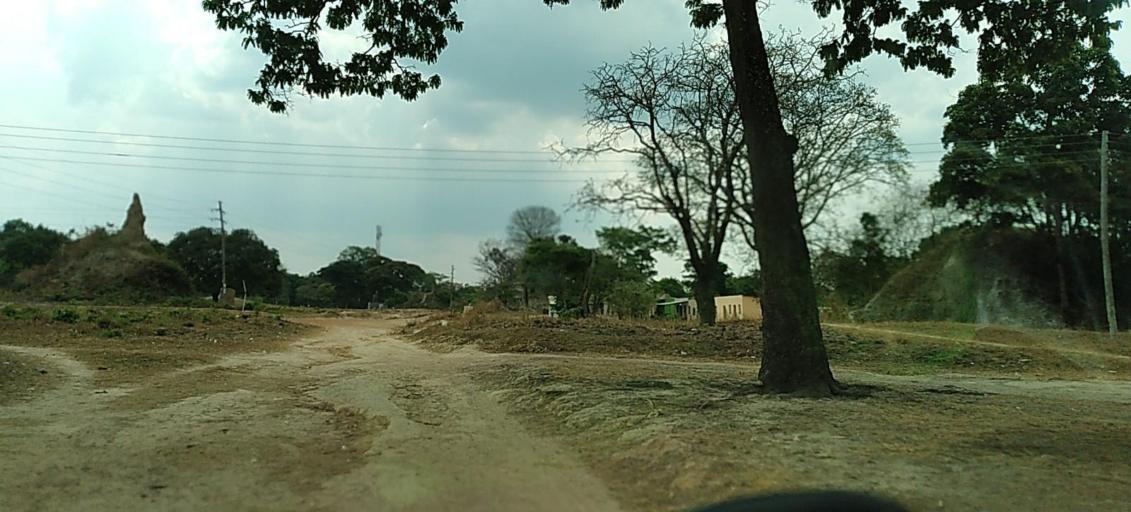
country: ZM
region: North-Western
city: Solwezi
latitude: -12.7866
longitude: 26.5173
